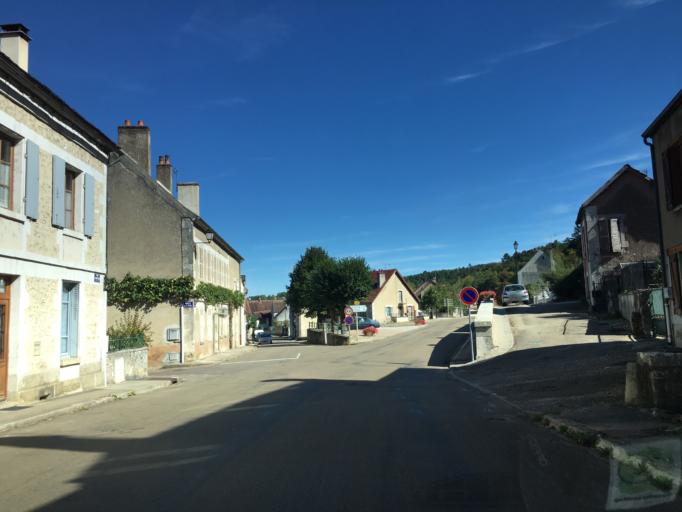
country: FR
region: Bourgogne
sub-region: Departement de l'Yonne
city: Vermenton
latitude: 47.5992
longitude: 3.6806
